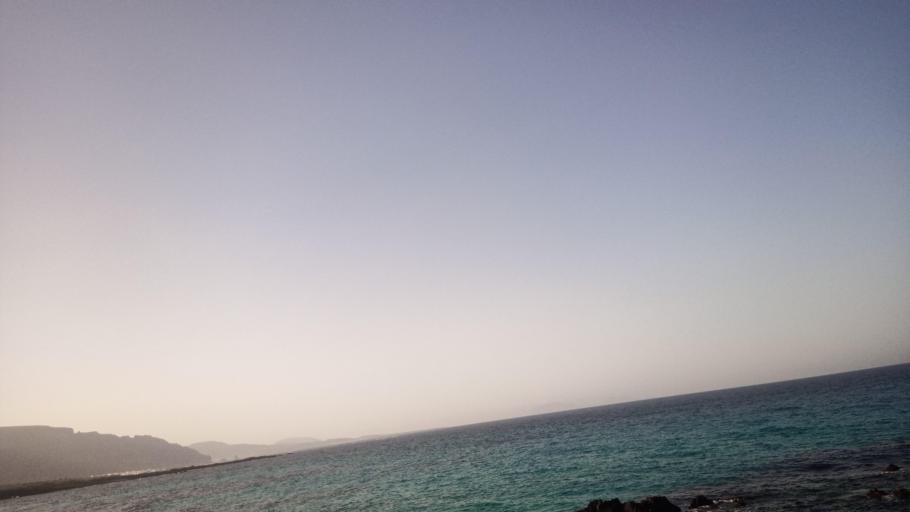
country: ES
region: Canary Islands
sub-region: Provincia de Las Palmas
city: Haria
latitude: 29.2088
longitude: -13.4278
